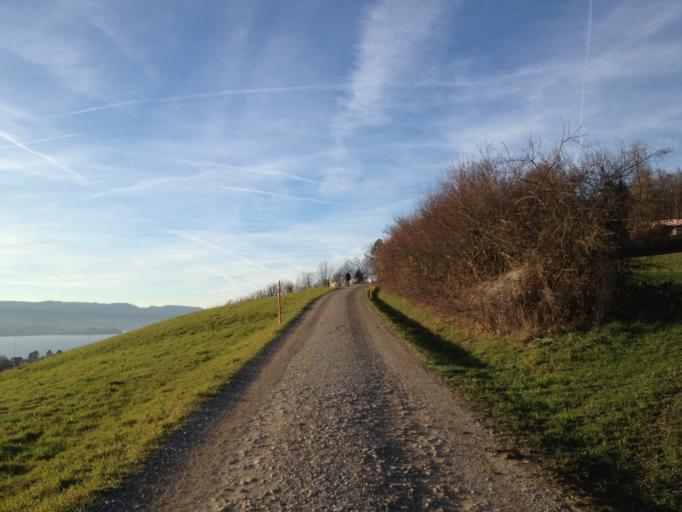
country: CH
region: Zurich
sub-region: Bezirk Meilen
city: Stafa
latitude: 47.2473
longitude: 8.7320
